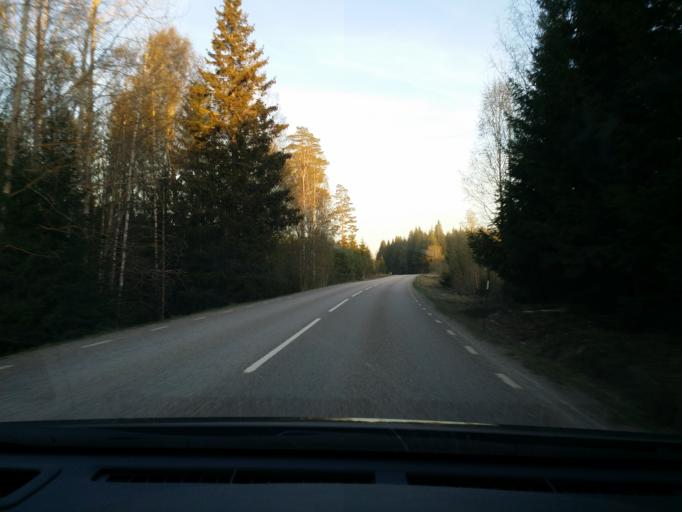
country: SE
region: Vaestmanland
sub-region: Sala Kommun
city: Sala
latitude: 59.8112
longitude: 16.5439
